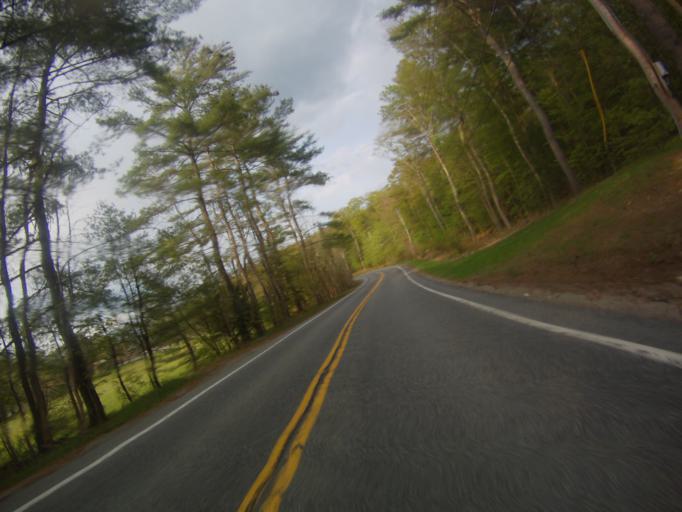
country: US
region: New York
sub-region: Warren County
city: Warrensburg
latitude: 43.6977
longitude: -73.7162
